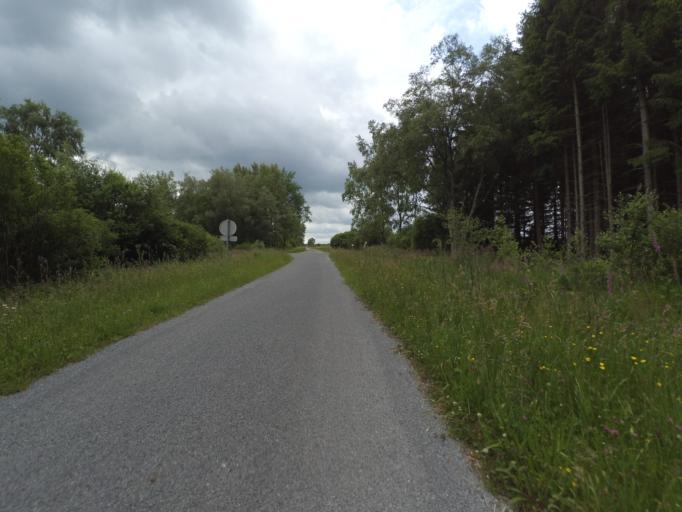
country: DE
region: North Rhine-Westphalia
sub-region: Regierungsbezirk Koln
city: Monschau
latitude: 50.5782
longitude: 6.1806
